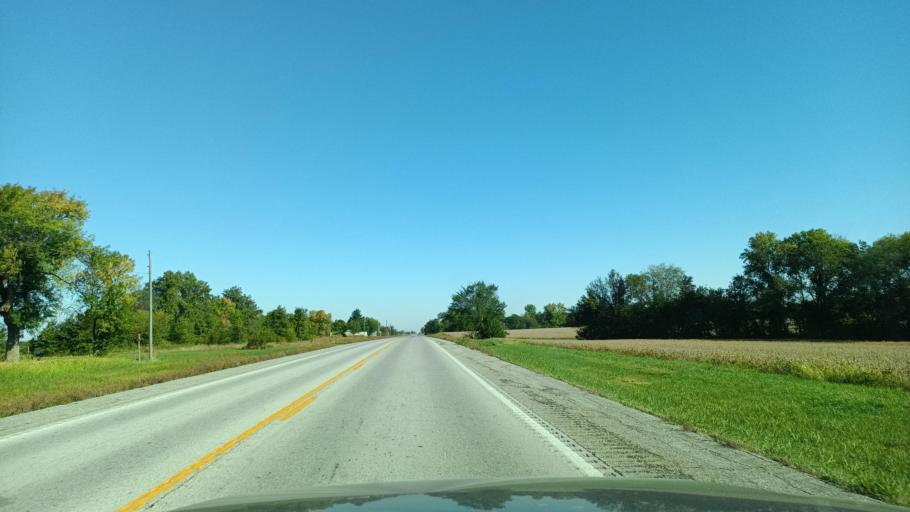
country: US
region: Missouri
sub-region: Audrain County
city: Vandalia
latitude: 39.3414
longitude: -91.6429
